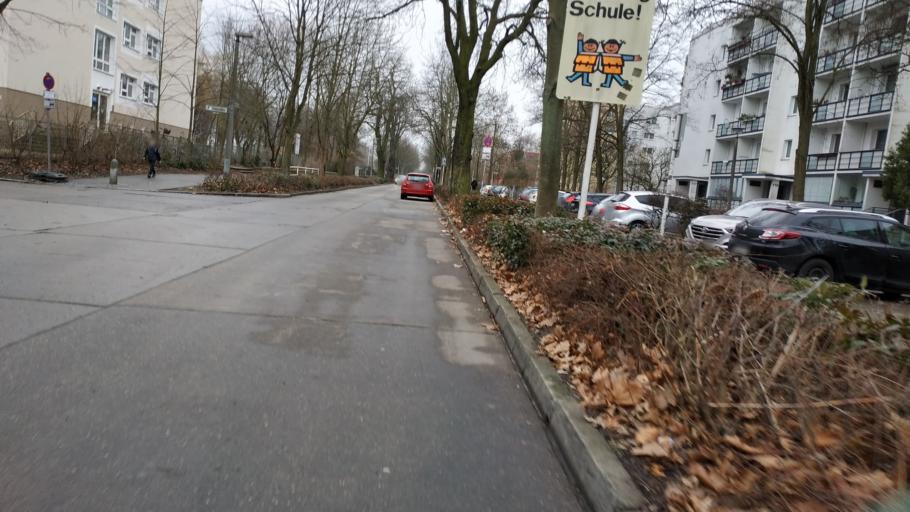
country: DE
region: Berlin
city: Hellersdorf
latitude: 52.5429
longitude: 13.5997
